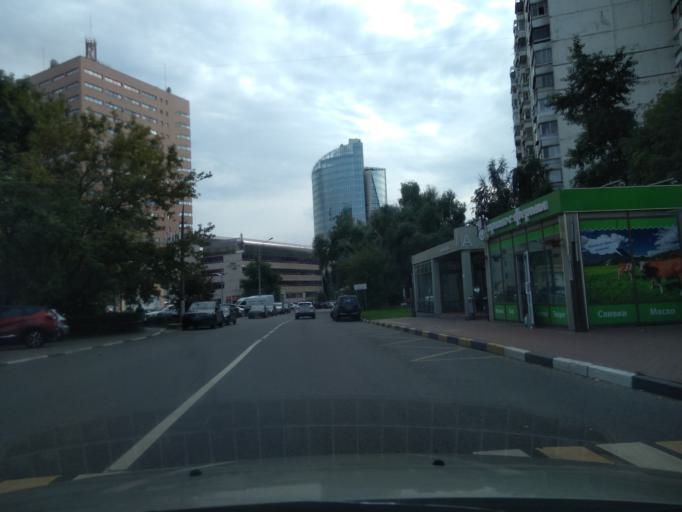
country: RU
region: Moscow
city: Khimki
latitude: 55.8821
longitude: 37.4304
